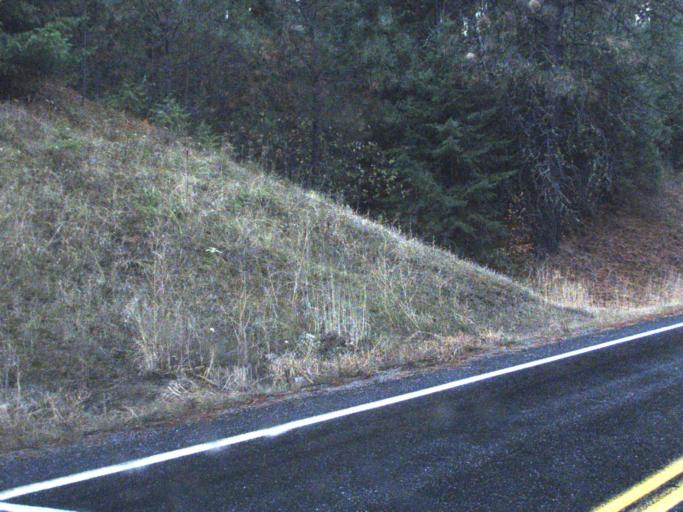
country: US
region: Washington
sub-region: Stevens County
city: Kettle Falls
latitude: 48.4851
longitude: -118.1698
